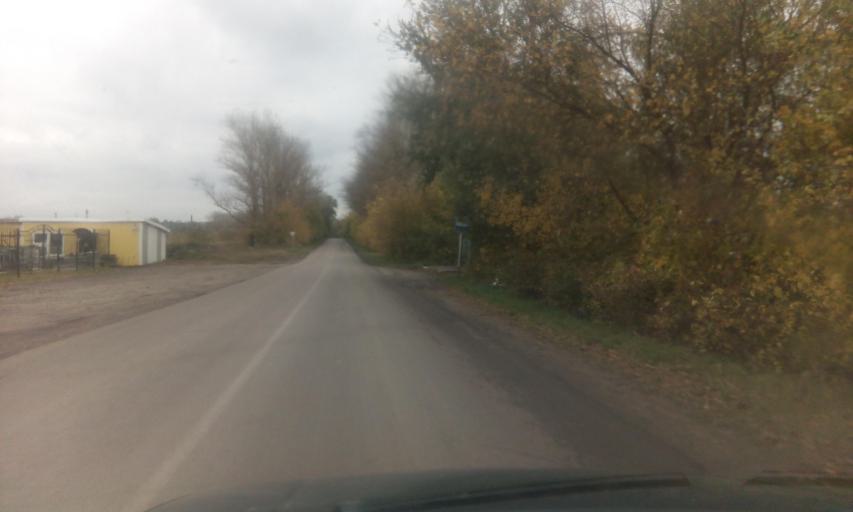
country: RU
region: Tula
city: Uzlovaya
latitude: 53.9741
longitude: 38.1373
